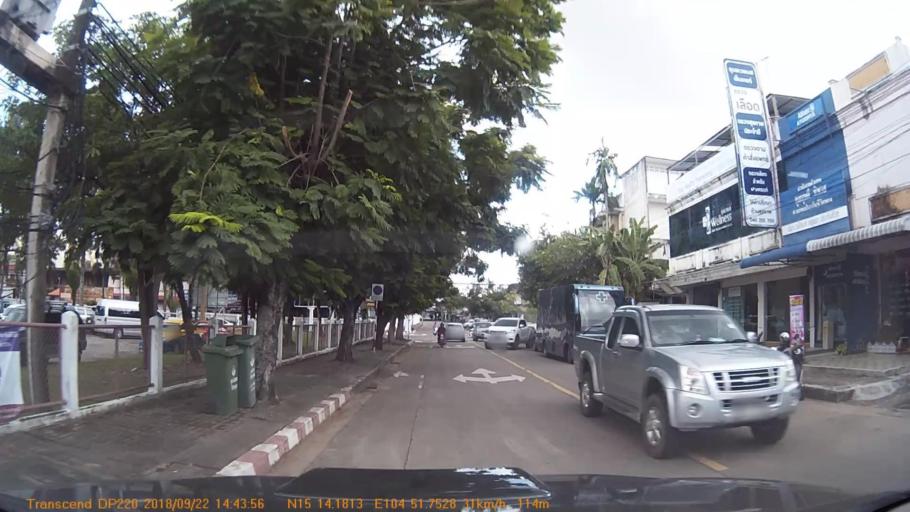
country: TH
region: Changwat Ubon Ratchathani
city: Ubon Ratchathani
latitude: 15.2362
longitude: 104.8625
